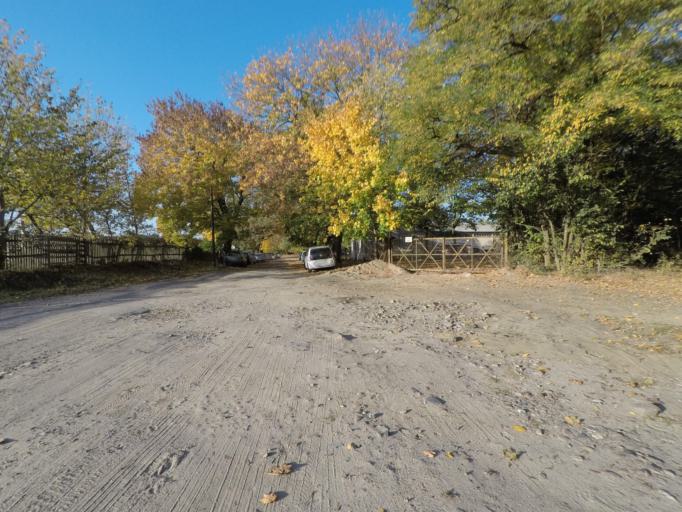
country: DE
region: Brandenburg
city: Biesenthal
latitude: 52.7767
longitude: 13.6416
